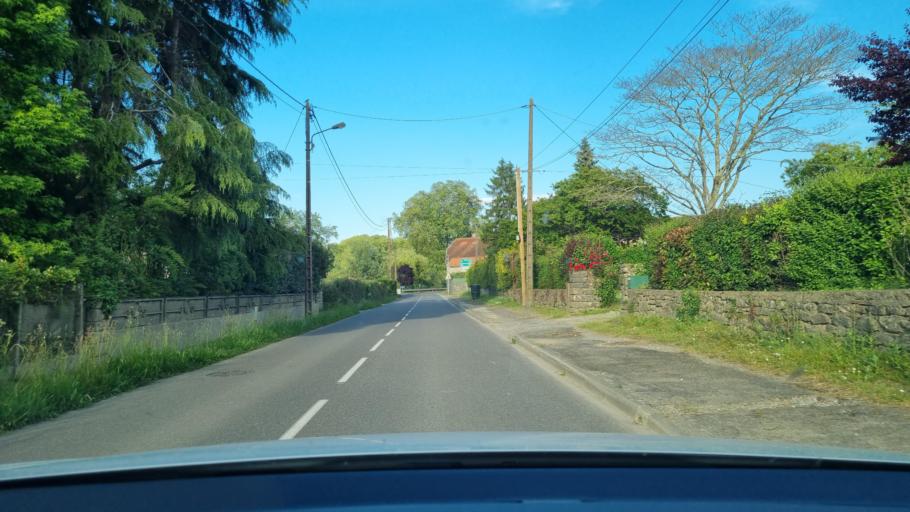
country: FR
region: Aquitaine
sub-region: Departement des Landes
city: Peyrehorade
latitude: 43.5424
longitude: -1.1084
